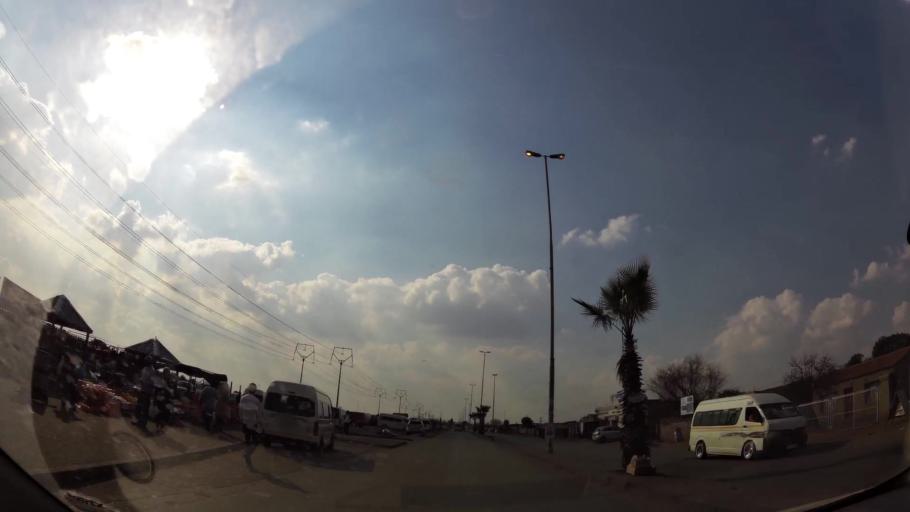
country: ZA
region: Gauteng
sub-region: Ekurhuleni Metropolitan Municipality
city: Germiston
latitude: -26.3262
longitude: 28.1472
